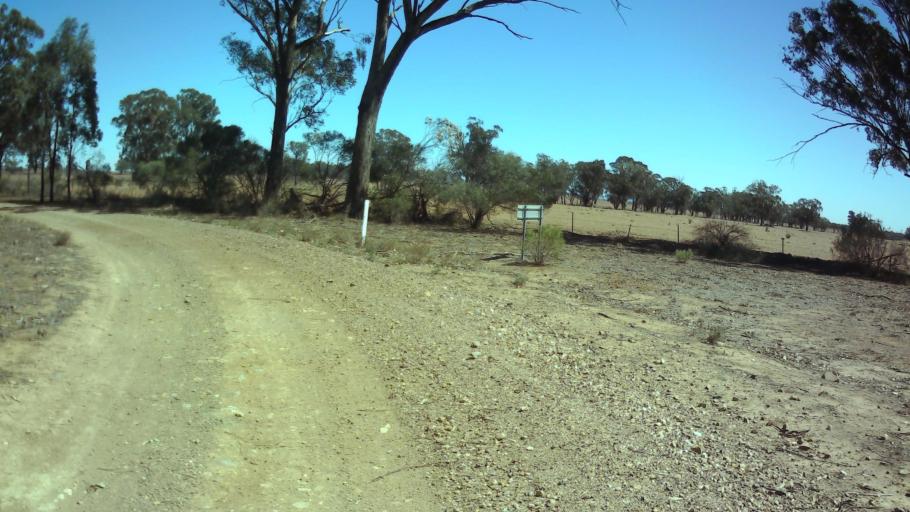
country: AU
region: New South Wales
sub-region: Forbes
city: Forbes
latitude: -33.6968
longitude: 147.8481
